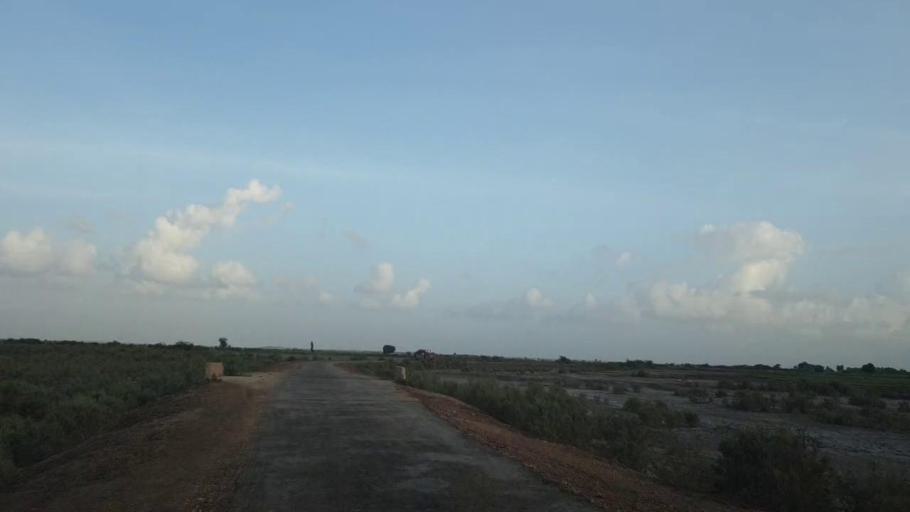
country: PK
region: Sindh
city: Kadhan
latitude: 24.5647
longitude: 69.1209
